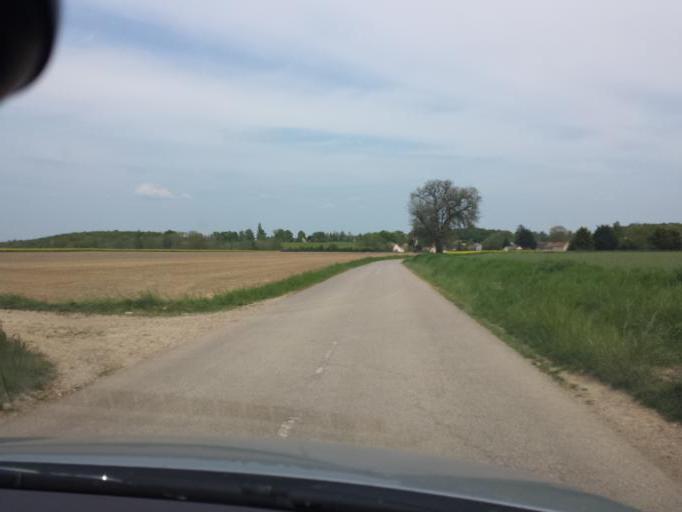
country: FR
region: Ile-de-France
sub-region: Departement des Yvelines
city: Longnes
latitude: 48.8620
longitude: 1.5997
